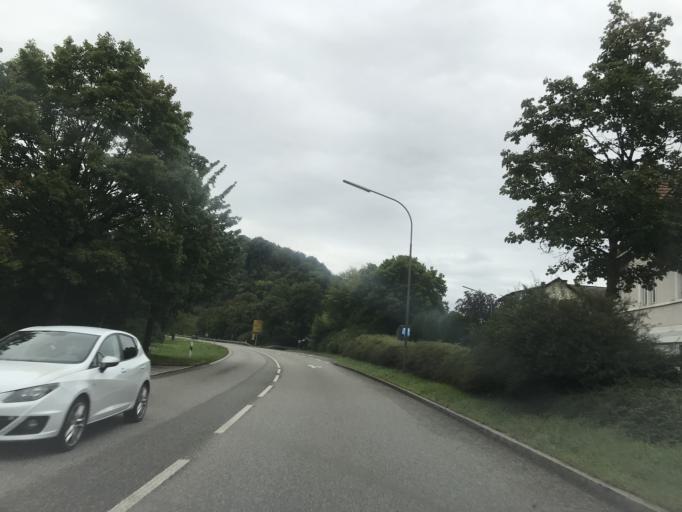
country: DE
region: Baden-Wuerttemberg
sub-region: Freiburg Region
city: Schworstadt
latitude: 47.5821
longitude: 7.9105
